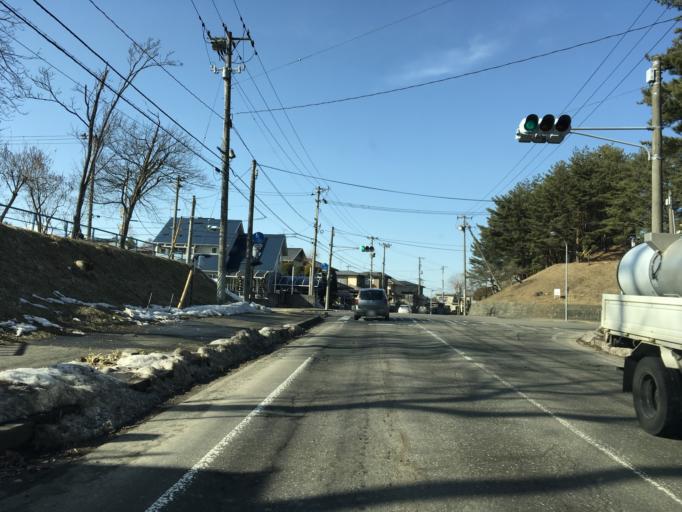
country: JP
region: Iwate
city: Morioka-shi
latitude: 39.7526
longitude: 141.1568
